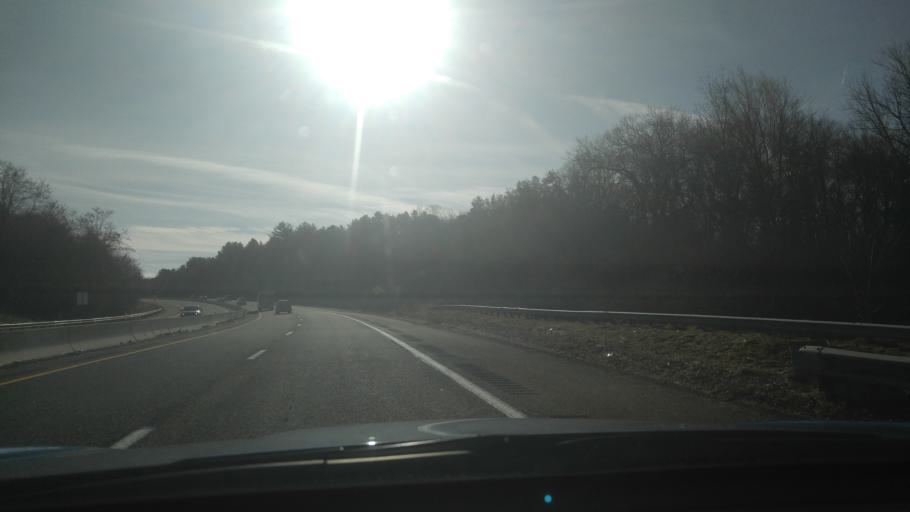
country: US
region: Rhode Island
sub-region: Providence County
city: Cumberland Hill
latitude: 41.9766
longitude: -71.4858
